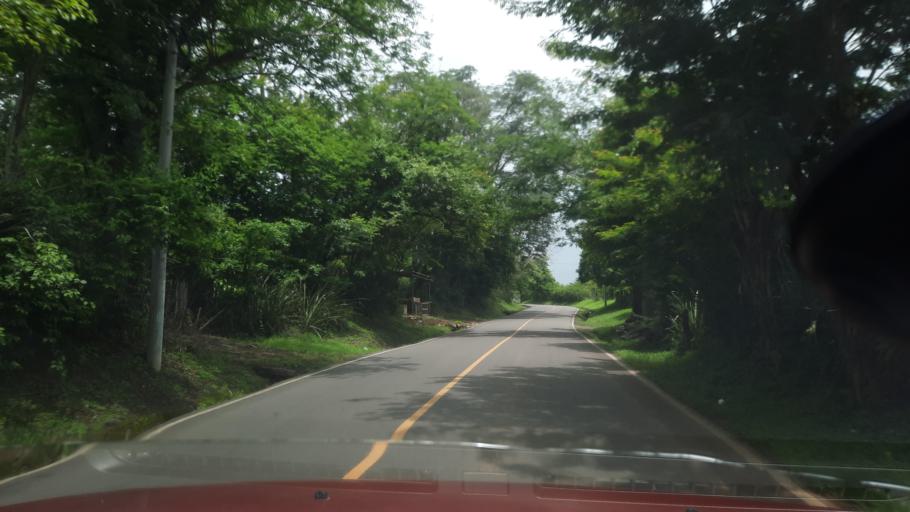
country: SV
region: La Union
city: Santa Rosa de Lima
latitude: 13.6457
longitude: -87.8569
